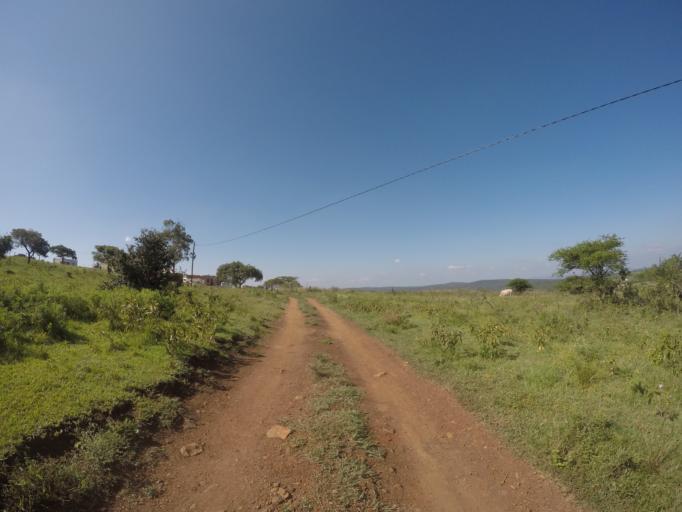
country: ZA
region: KwaZulu-Natal
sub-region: uThungulu District Municipality
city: Empangeni
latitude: -28.5708
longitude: 31.7199
